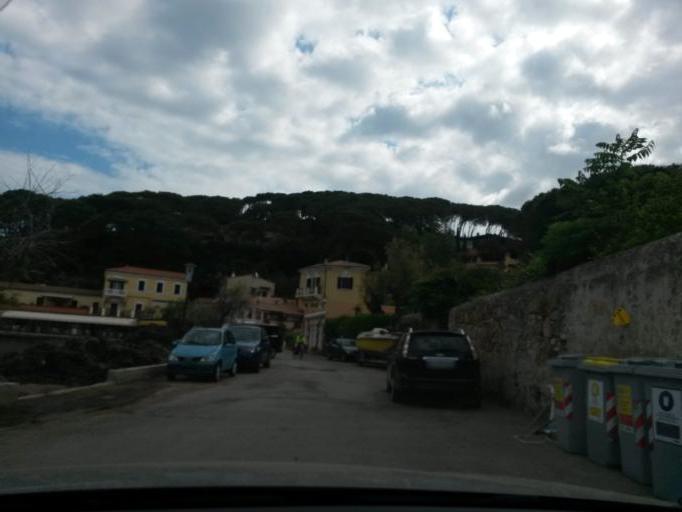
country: IT
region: Tuscany
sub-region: Provincia di Livorno
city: Rio nell'Elba
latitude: 42.7992
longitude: 10.3576
